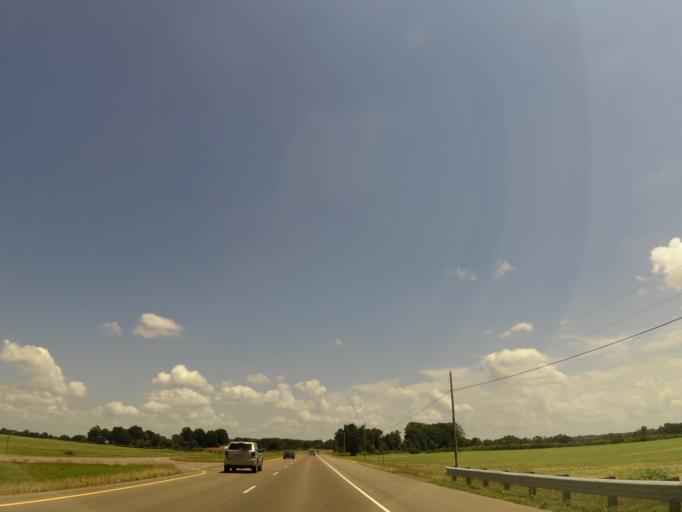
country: US
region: Tennessee
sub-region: Crockett County
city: Alamo
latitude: 35.8549
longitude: -89.2001
